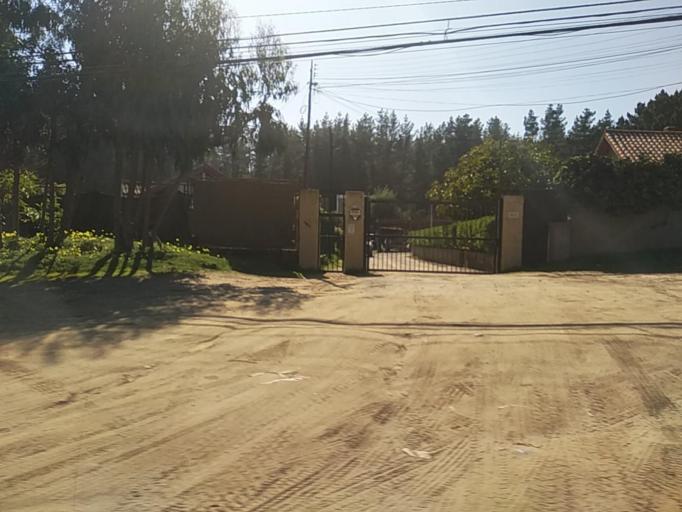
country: CL
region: Valparaiso
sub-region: Provincia de Valparaiso
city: Vina del Mar
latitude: -32.9591
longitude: -71.5377
